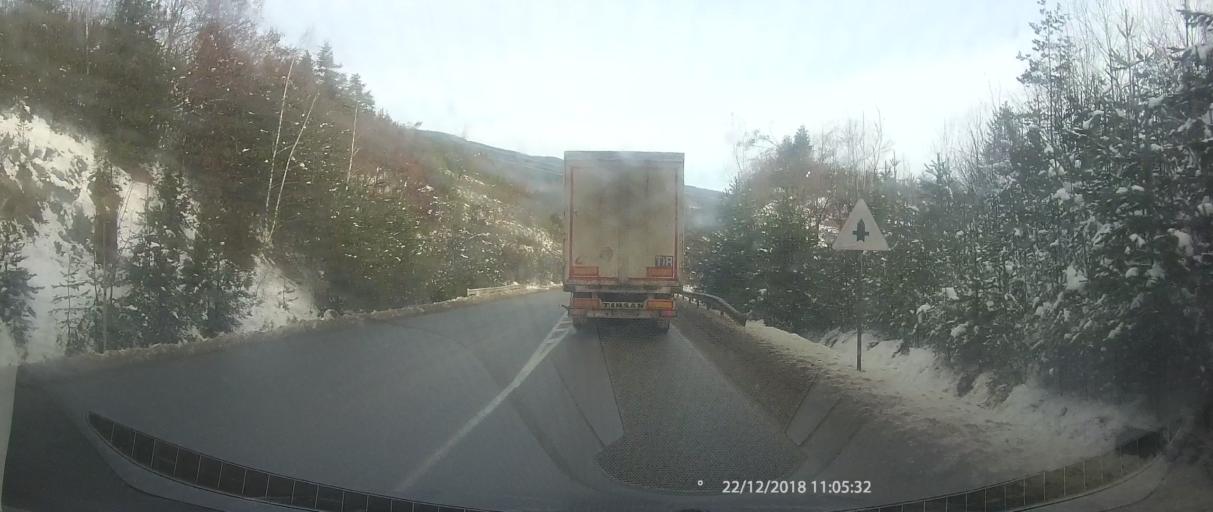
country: BG
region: Kyustendil
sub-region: Obshtina Kyustendil
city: Kyustendil
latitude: 42.2643
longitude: 22.5772
